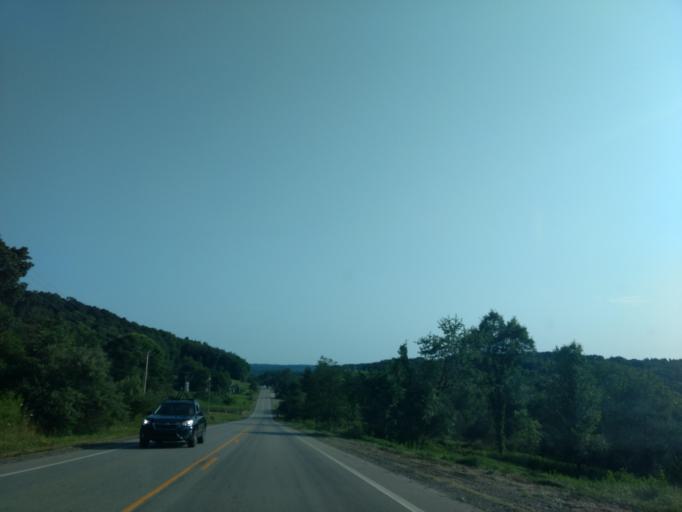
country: US
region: Pennsylvania
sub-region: Butler County
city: Zelienople
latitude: 40.8309
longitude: -80.1223
